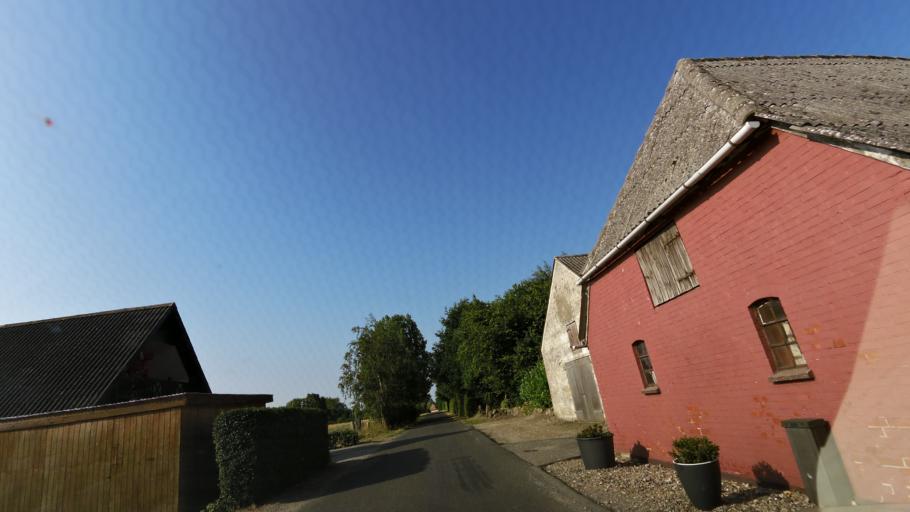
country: DK
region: South Denmark
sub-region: Nordfyns Kommune
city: Otterup
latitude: 55.5434
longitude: 10.4081
